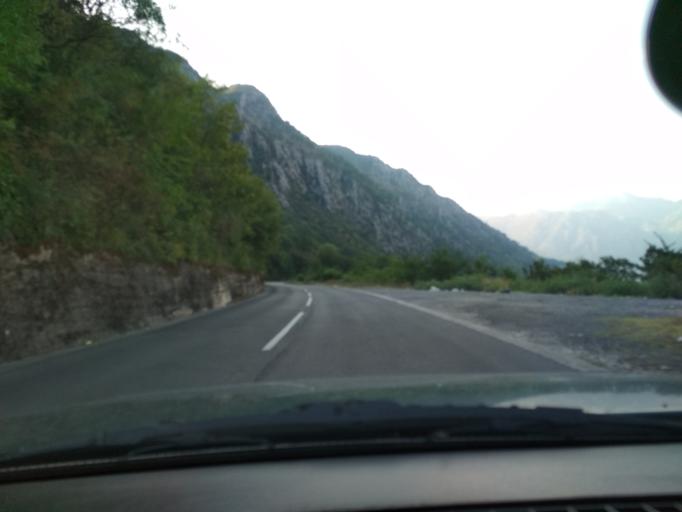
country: ME
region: Kotor
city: Kotor
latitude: 42.4119
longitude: 18.7637
